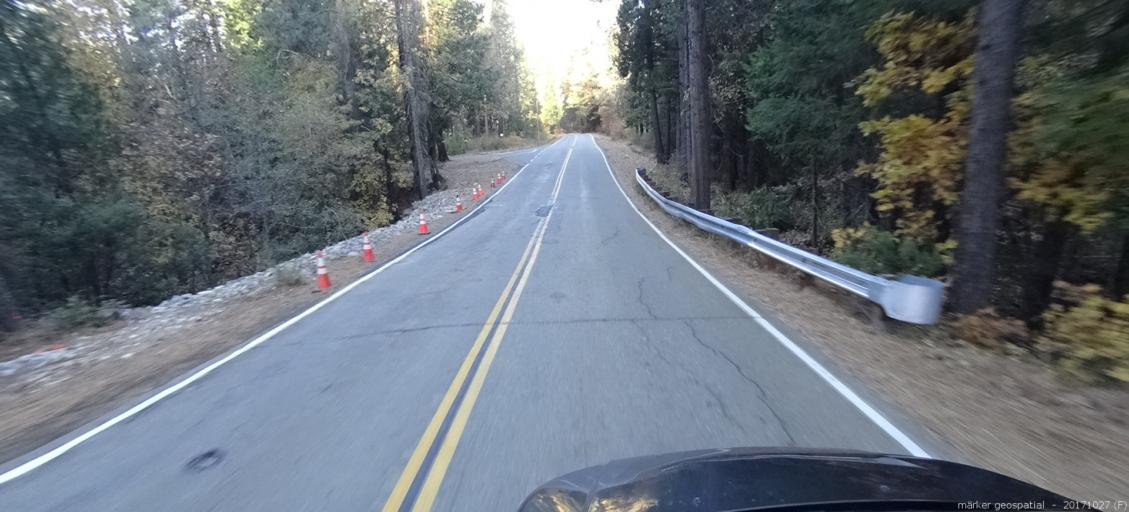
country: US
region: California
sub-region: Shasta County
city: Burney
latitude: 40.9326
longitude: -121.9460
